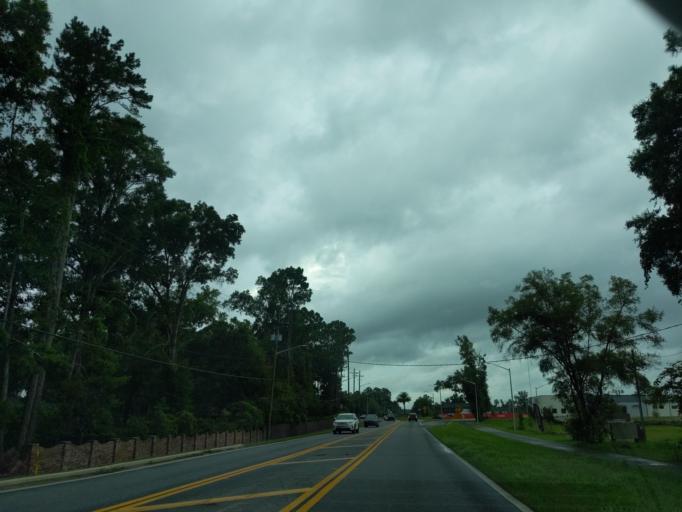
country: US
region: Florida
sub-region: Alachua County
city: Gainesville
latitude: 29.6362
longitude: -82.4224
